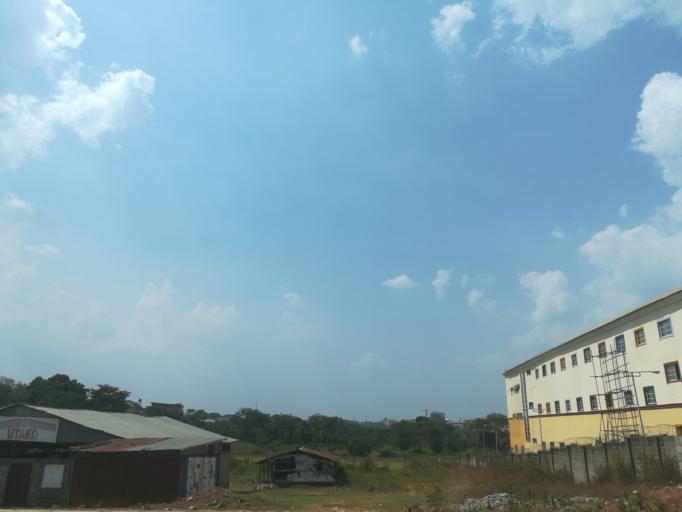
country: NG
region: Abuja Federal Capital Territory
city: Abuja
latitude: 9.0584
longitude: 7.4445
